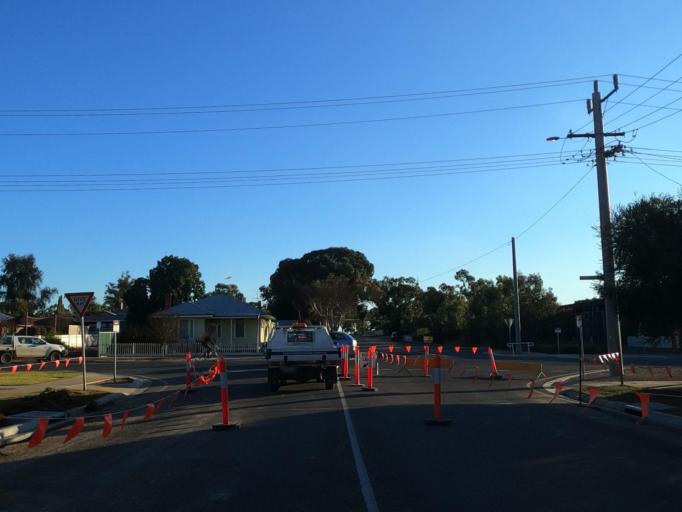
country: AU
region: Victoria
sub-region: Swan Hill
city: Swan Hill
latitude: -35.3352
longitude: 143.5574
